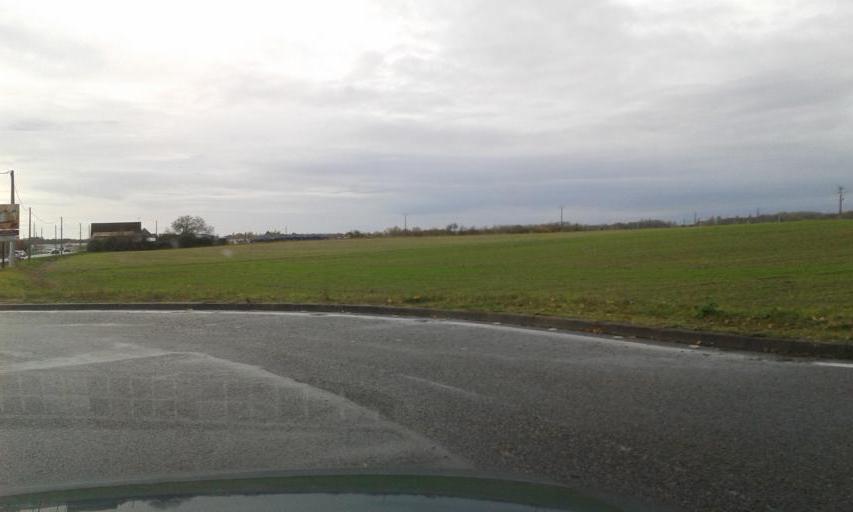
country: FR
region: Centre
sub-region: Departement du Loiret
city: Saint-Ay
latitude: 47.8471
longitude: 1.7253
